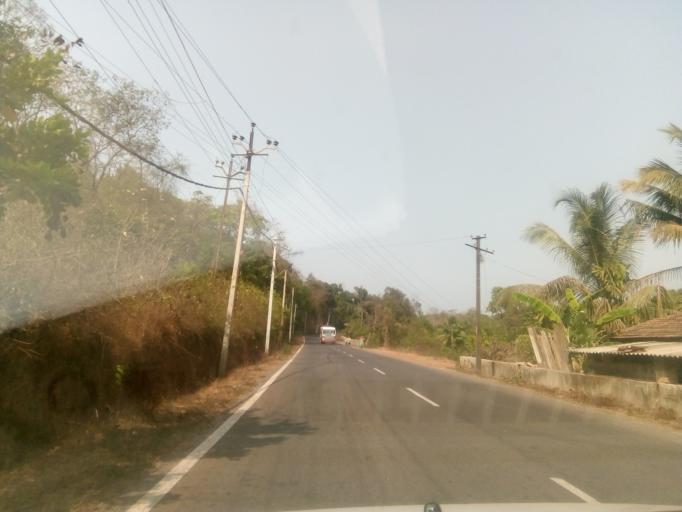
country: IN
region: Goa
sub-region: North Goa
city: Pernem
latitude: 15.7045
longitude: 73.8507
